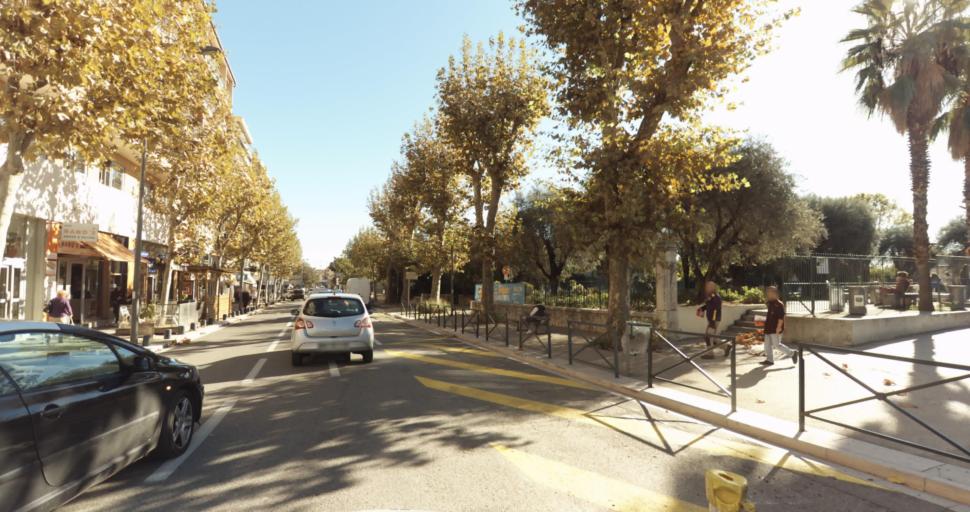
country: FR
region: Provence-Alpes-Cote d'Azur
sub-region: Departement des Alpes-Maritimes
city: Vence
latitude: 43.7234
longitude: 7.1059
